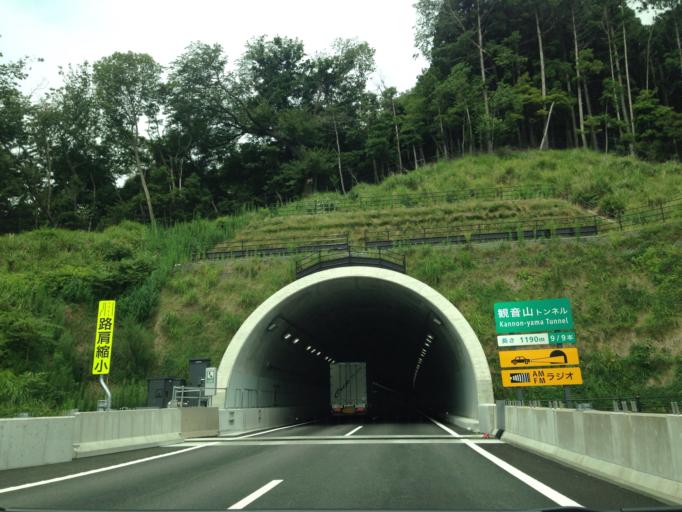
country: JP
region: Aichi
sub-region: Tokai-shi
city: Toyokawa
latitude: 34.8839
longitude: 137.3699
